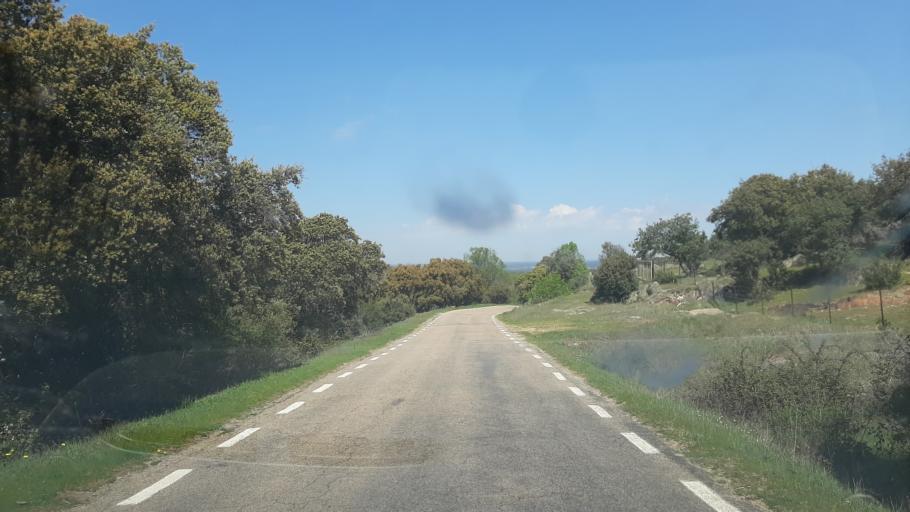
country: ES
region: Castille and Leon
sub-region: Provincia de Salamanca
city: Navarredonda de la Rinconada
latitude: 40.6178
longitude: -6.0199
